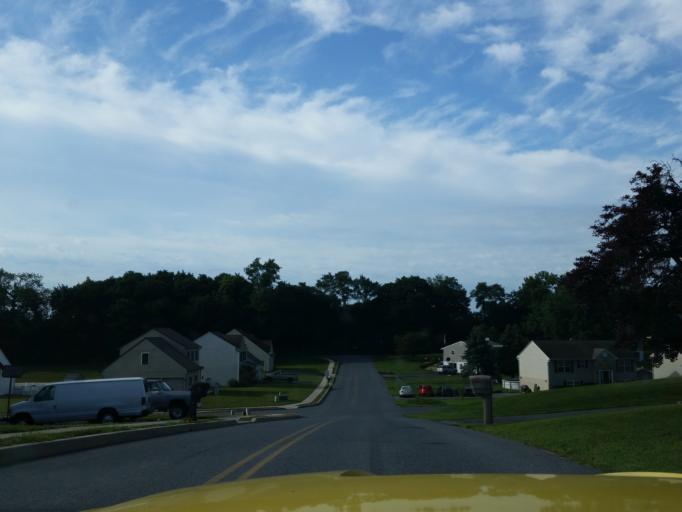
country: US
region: Pennsylvania
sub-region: Lebanon County
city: Jonestown
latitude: 40.4209
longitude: -76.4728
